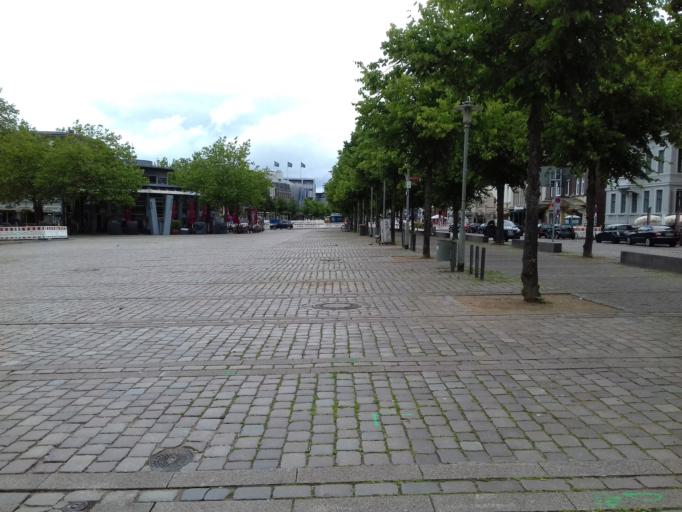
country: DE
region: Schleswig-Holstein
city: Neumunster
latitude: 54.0708
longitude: 9.9873
